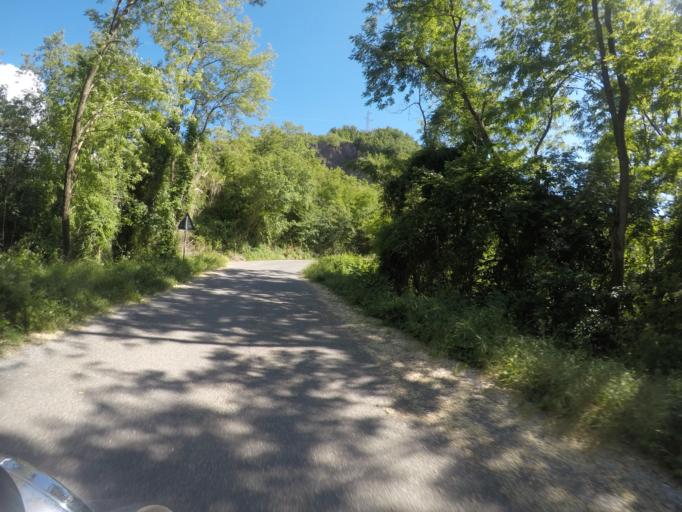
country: IT
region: Tuscany
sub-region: Provincia di Massa-Carrara
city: Fosdinovo
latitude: 44.1357
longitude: 10.0751
